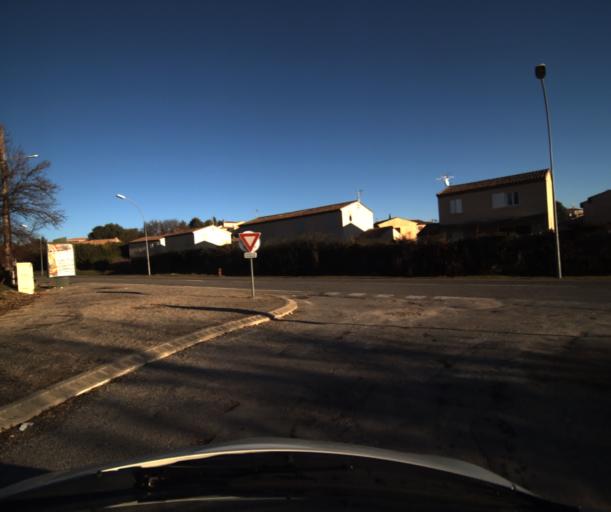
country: FR
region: Provence-Alpes-Cote d'Azur
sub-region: Departement du Vaucluse
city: Pertuis
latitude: 43.7018
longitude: 5.4985
